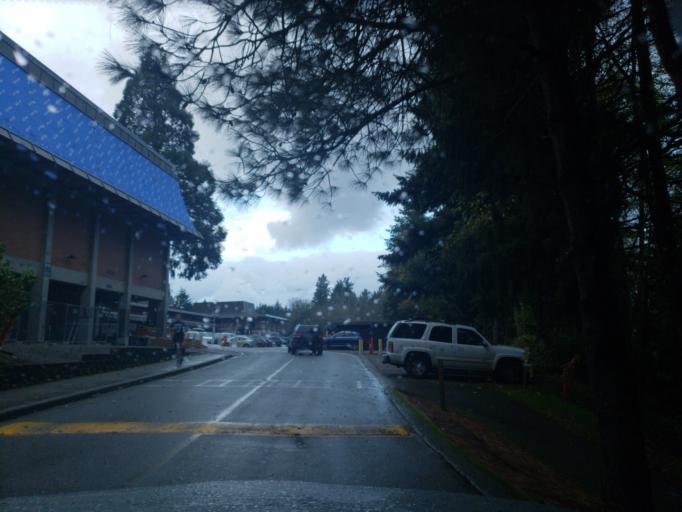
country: US
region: Washington
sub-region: King County
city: Shoreline
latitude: 47.7493
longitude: -122.3585
